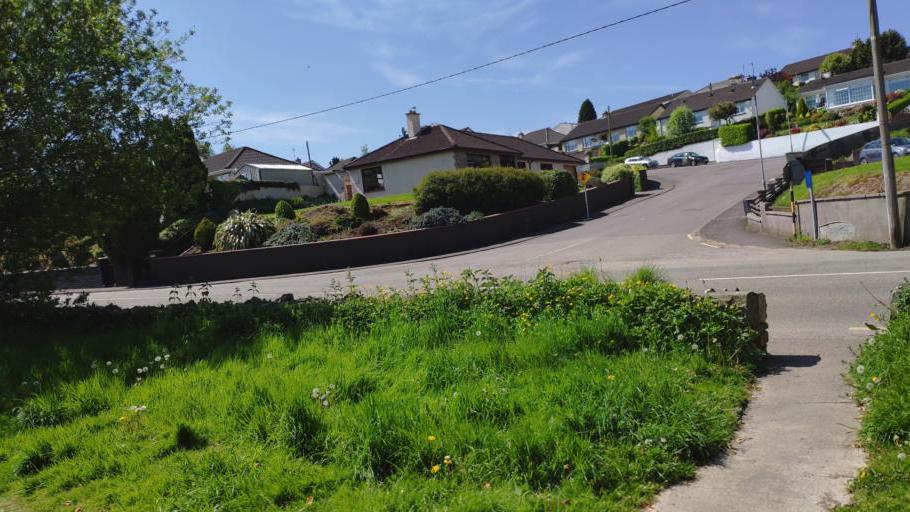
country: IE
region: Munster
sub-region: County Cork
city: Blarney
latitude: 51.9374
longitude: -8.5632
